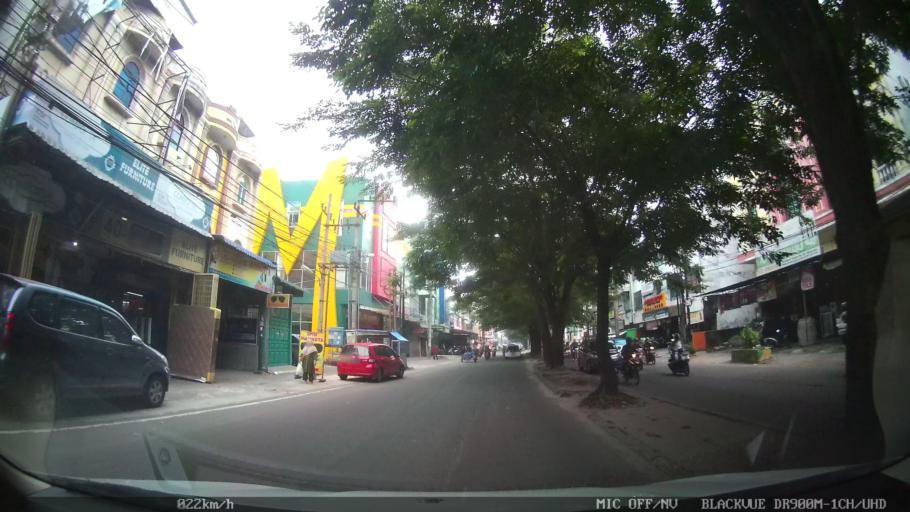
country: ID
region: North Sumatra
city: Medan
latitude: 3.5503
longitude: 98.6885
